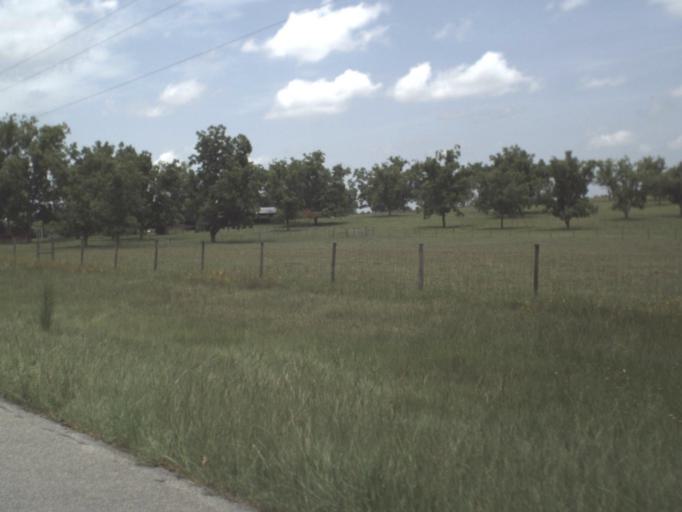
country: US
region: Florida
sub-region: Madison County
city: Madison
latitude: 30.5034
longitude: -83.4237
